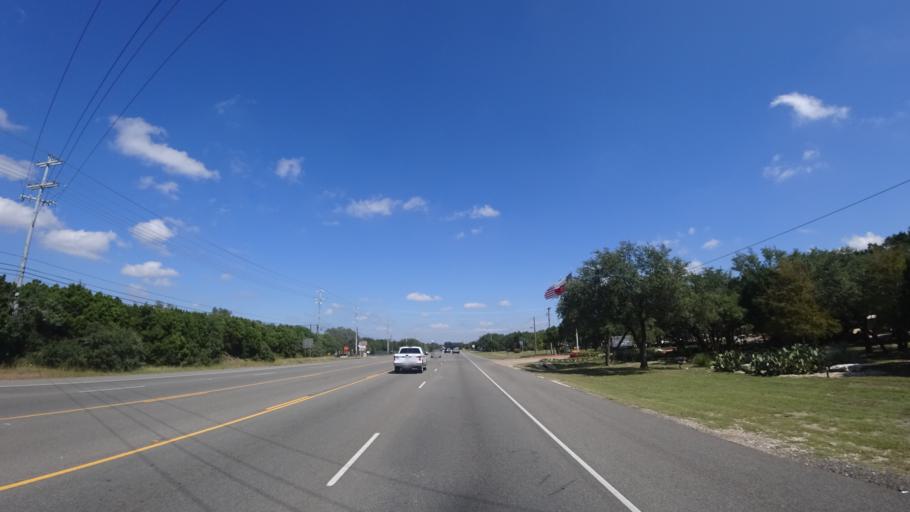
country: US
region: Texas
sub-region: Williamson County
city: Anderson Mill
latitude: 30.4377
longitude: -97.8379
